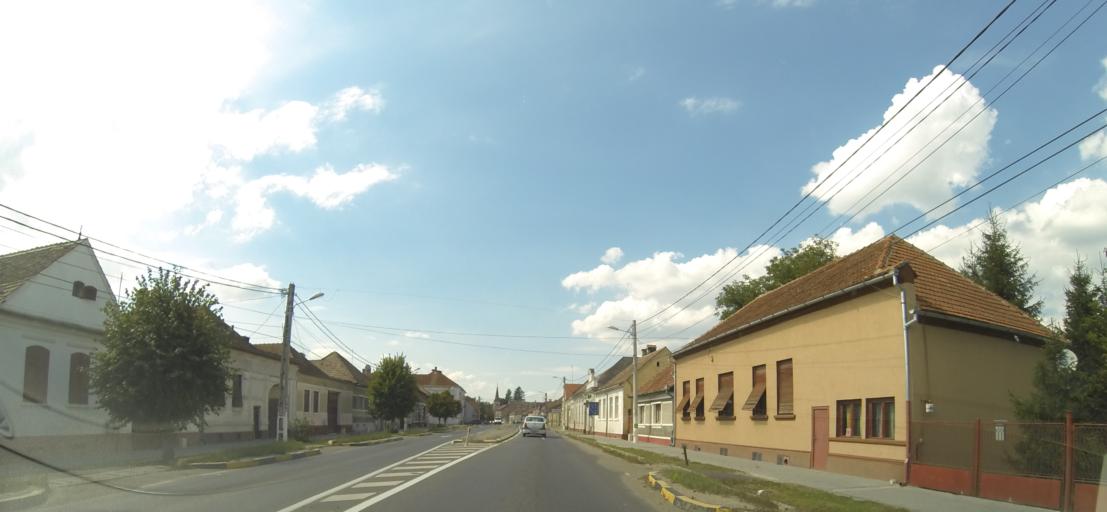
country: RO
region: Brasov
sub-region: Comuna Sercaia
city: Sercaia
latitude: 45.8303
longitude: 25.1421
